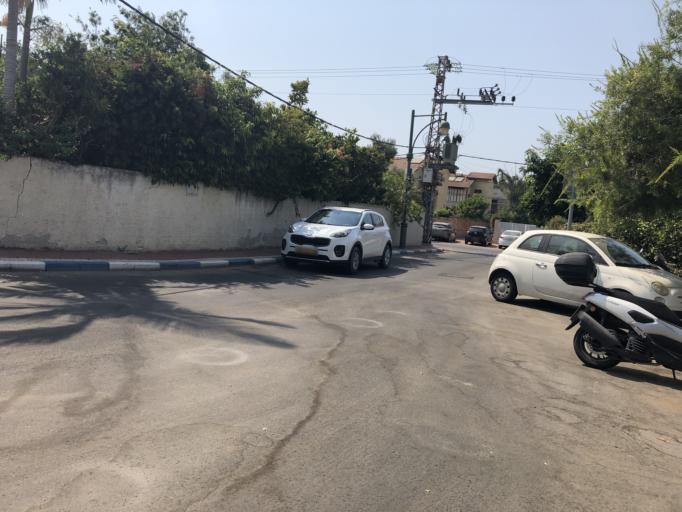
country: IL
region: Tel Aviv
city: Bene Beraq
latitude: 32.0550
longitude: 34.8326
